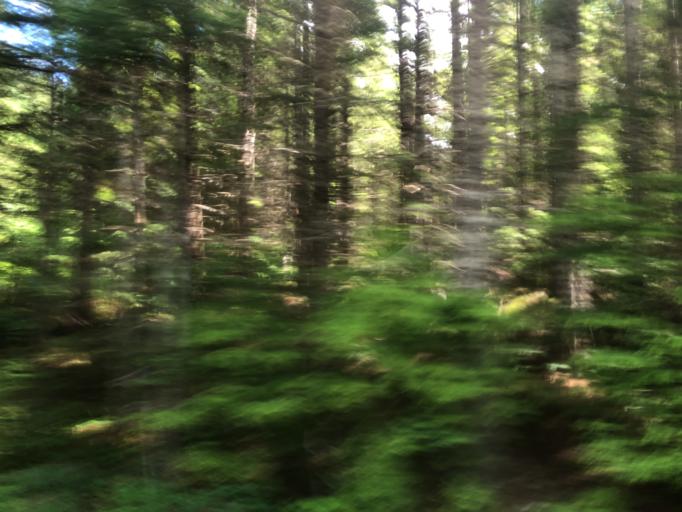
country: US
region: Oregon
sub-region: Clackamas County
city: Mount Hood Village
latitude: 45.4686
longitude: -121.8537
